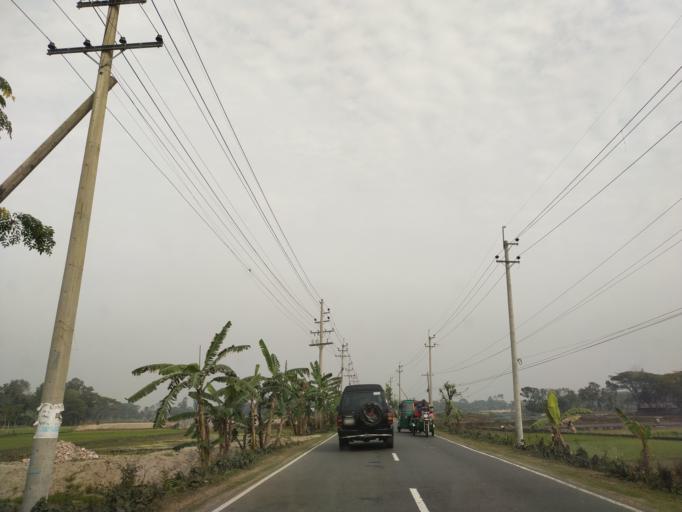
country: BD
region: Dhaka
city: Narsingdi
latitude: 23.9893
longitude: 90.7359
